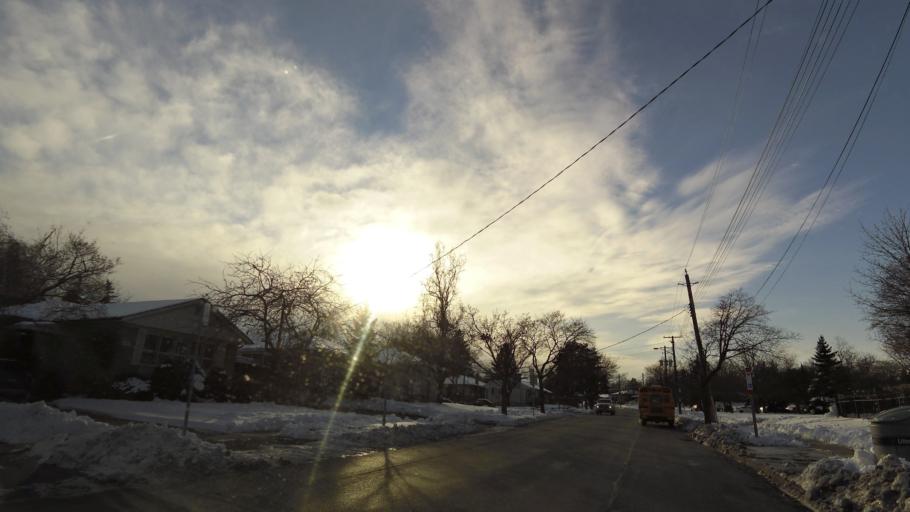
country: CA
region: Ontario
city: Etobicoke
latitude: 43.6663
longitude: -79.5793
